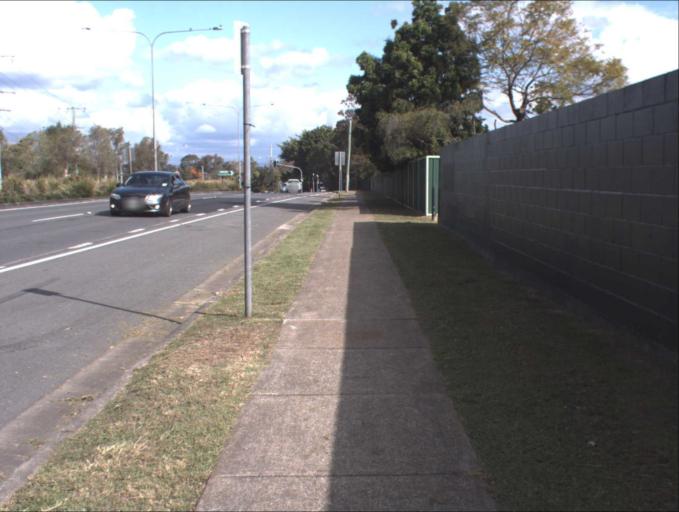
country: AU
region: Queensland
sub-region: Logan
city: Waterford West
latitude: -27.6847
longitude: 153.1220
